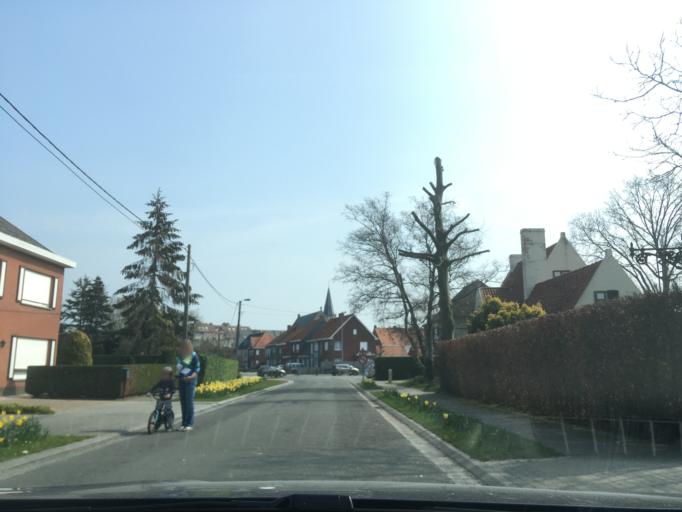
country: BE
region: Flanders
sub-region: Provincie West-Vlaanderen
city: Ardooie
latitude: 50.9796
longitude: 3.1940
